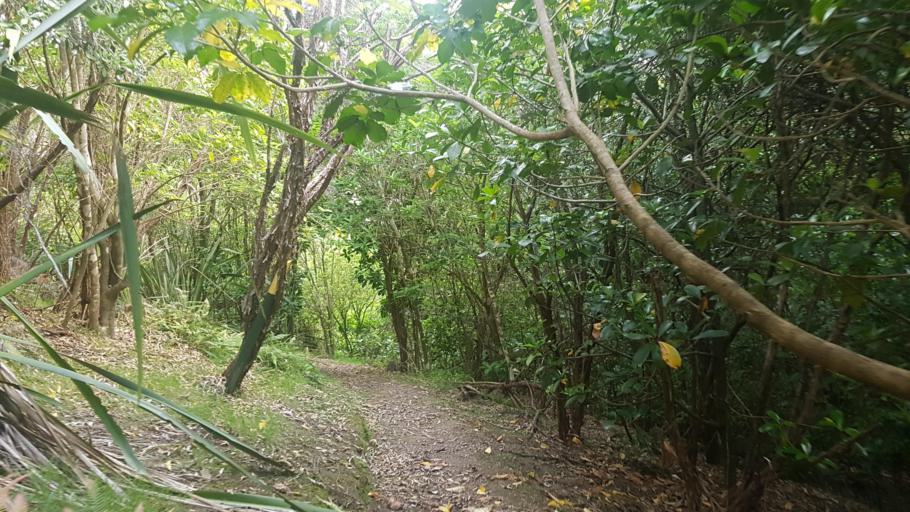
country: NZ
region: Auckland
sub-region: Auckland
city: Pakuranga
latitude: -36.7773
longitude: 175.0016
